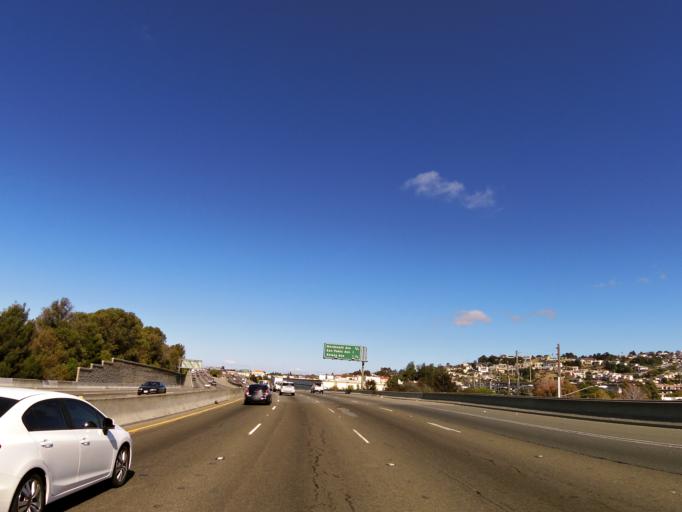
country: US
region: California
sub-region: Contra Costa County
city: El Cerrito
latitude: 37.9206
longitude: -122.3178
